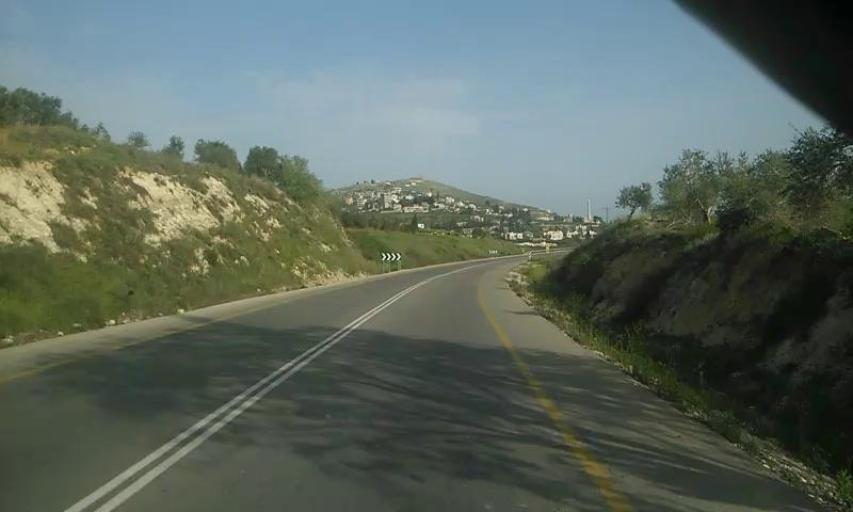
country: PS
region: West Bank
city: Madama
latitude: 32.1836
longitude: 35.2399
